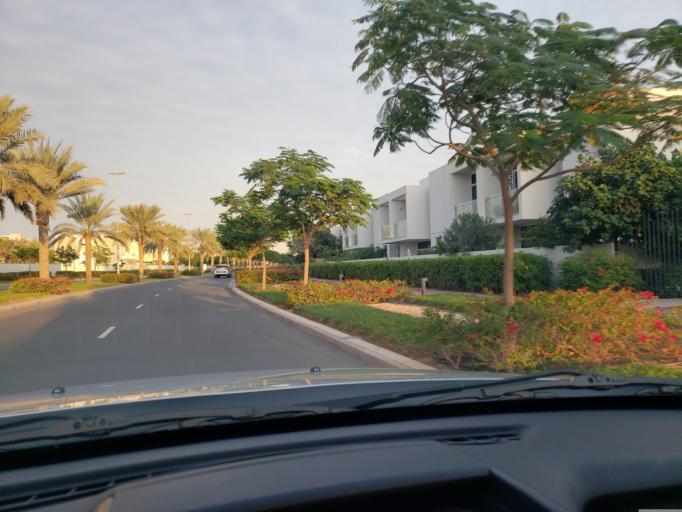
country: AE
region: Dubai
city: Dubai
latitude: 25.0193
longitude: 55.2697
